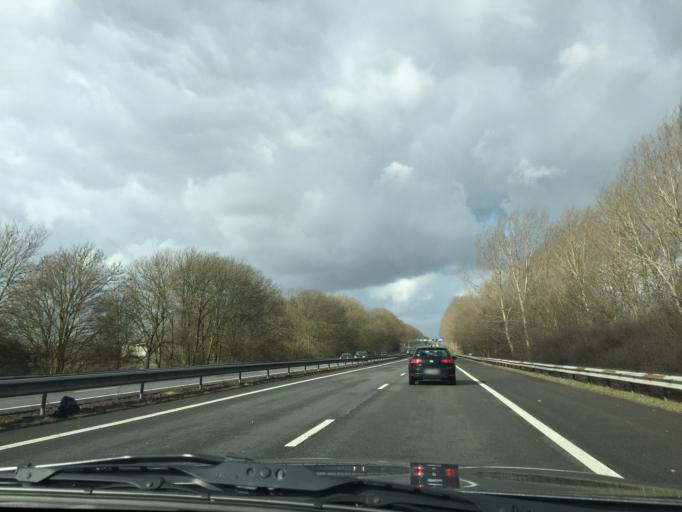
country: NL
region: Gelderland
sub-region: Gemeente Zevenaar
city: Zevenaar
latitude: 51.9286
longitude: 6.1109
